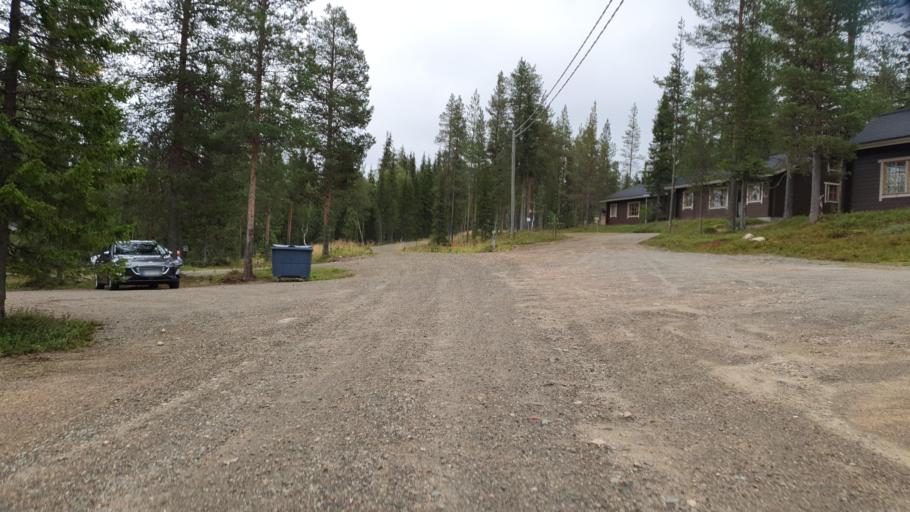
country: FI
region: Lapland
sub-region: Tunturi-Lappi
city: Kolari
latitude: 67.5991
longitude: 24.1957
